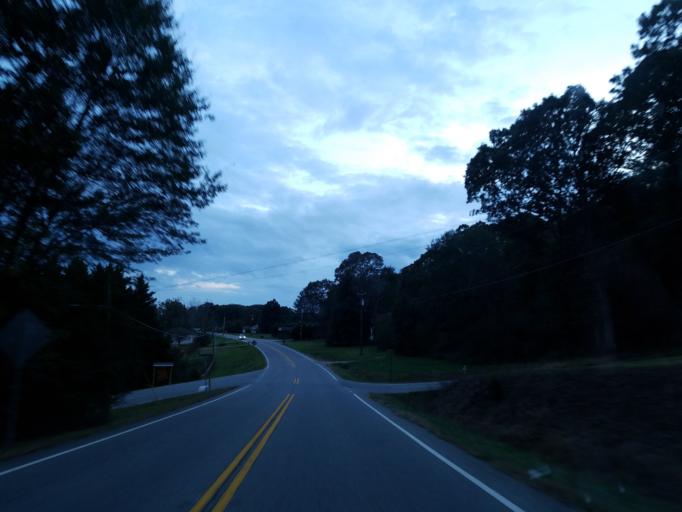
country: US
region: Georgia
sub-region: Dawson County
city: Dawsonville
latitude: 34.3233
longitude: -84.1061
